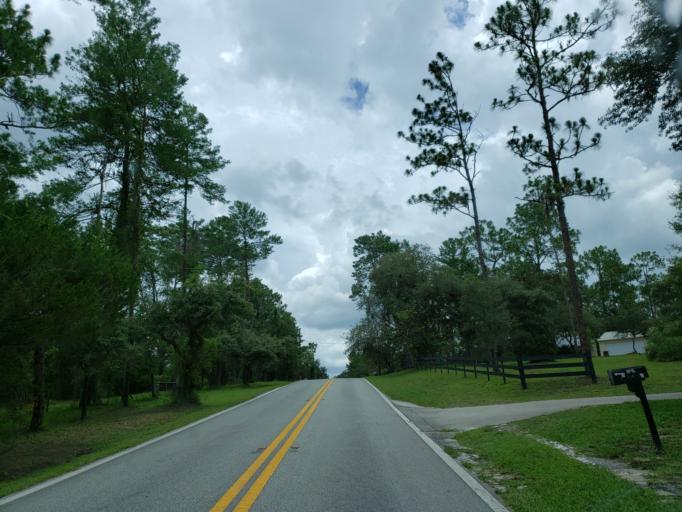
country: US
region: Florida
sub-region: Citrus County
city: Floral City
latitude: 28.6633
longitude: -82.3166
